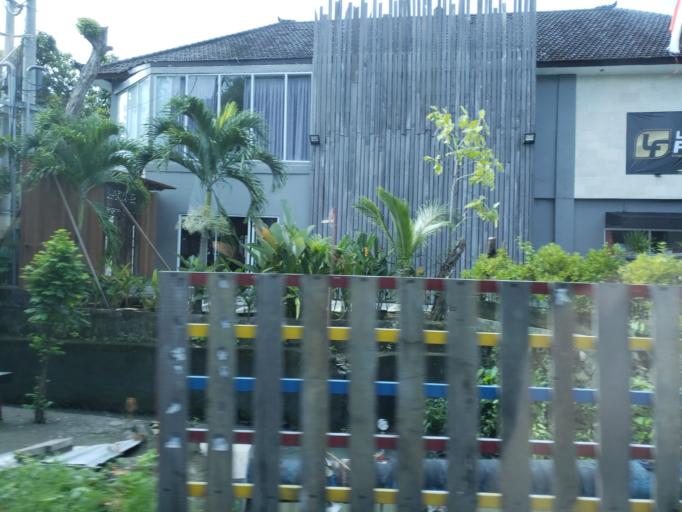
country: ID
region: Bali
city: Kuta
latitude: -8.6832
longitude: 115.1731
